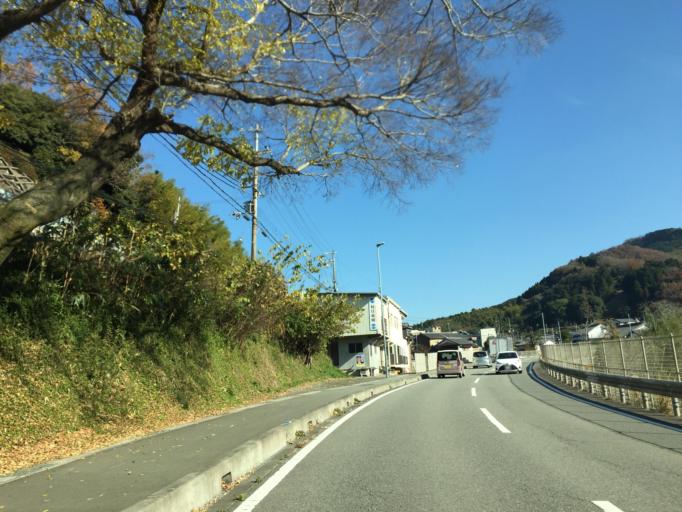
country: JP
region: Wakayama
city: Iwade
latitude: 34.1658
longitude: 135.3021
